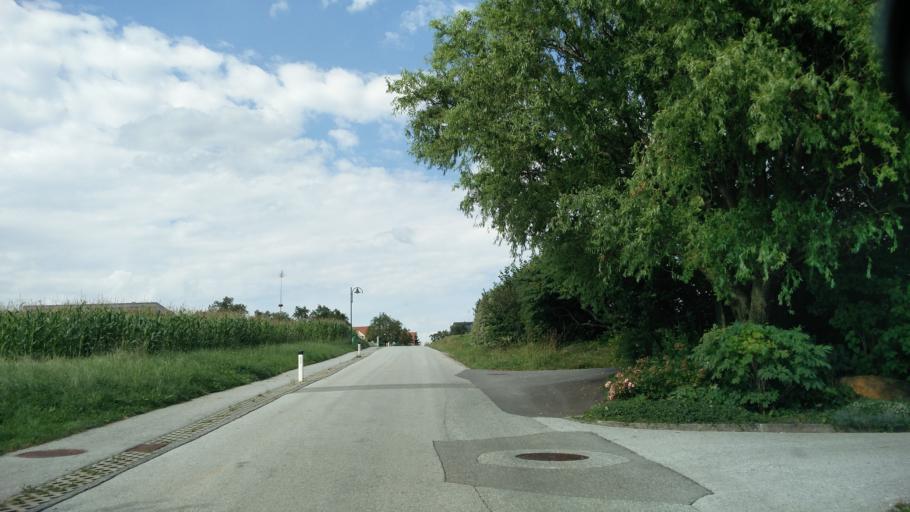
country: AT
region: Styria
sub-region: Politischer Bezirk Weiz
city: Weiz
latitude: 47.2148
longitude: 15.6066
